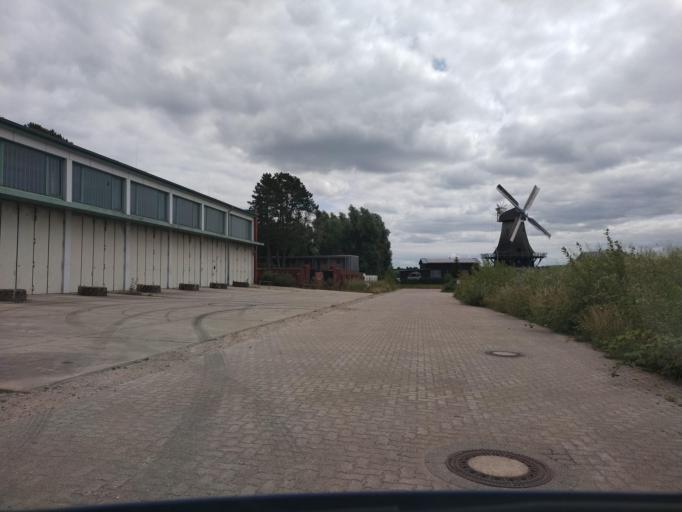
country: DE
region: Schleswig-Holstein
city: Fahrdorf
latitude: 54.5196
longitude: 9.5948
